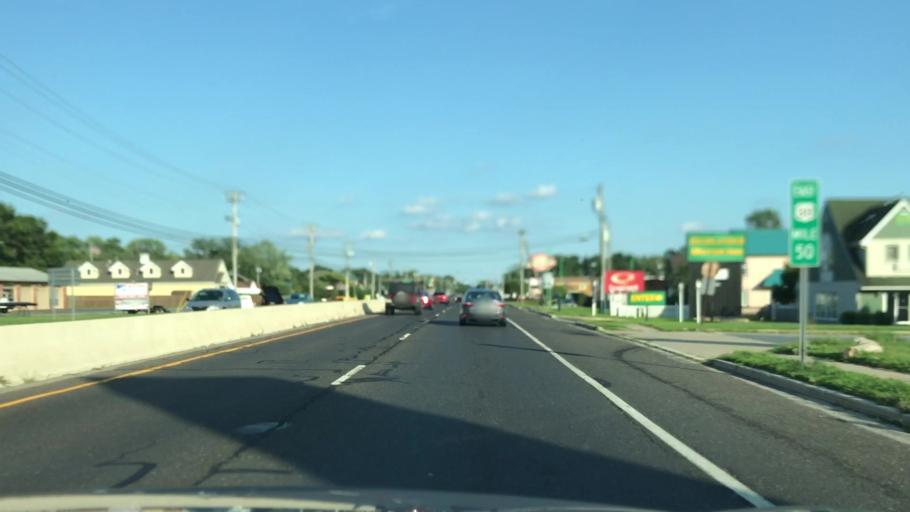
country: US
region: New Jersey
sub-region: Atlantic County
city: Absecon
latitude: 39.4441
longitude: -74.5256
